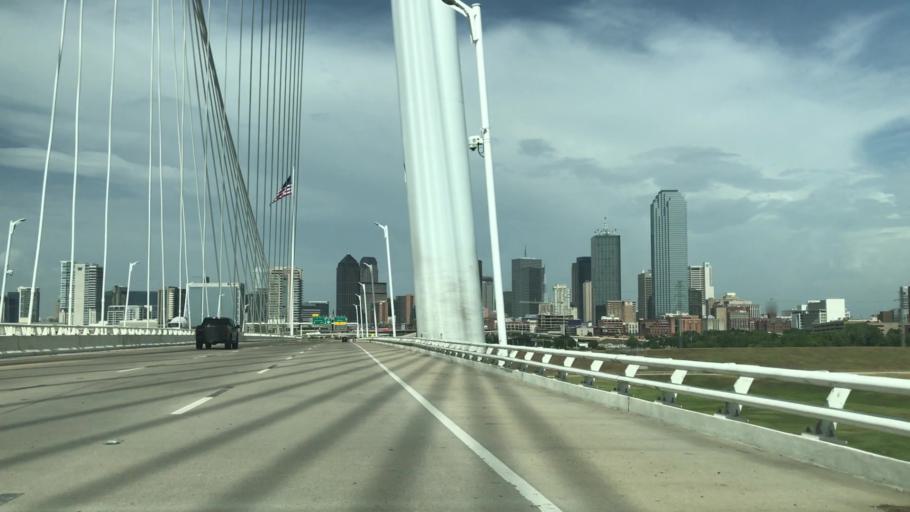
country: US
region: Texas
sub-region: Dallas County
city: Dallas
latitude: 32.7797
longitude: -96.8226
